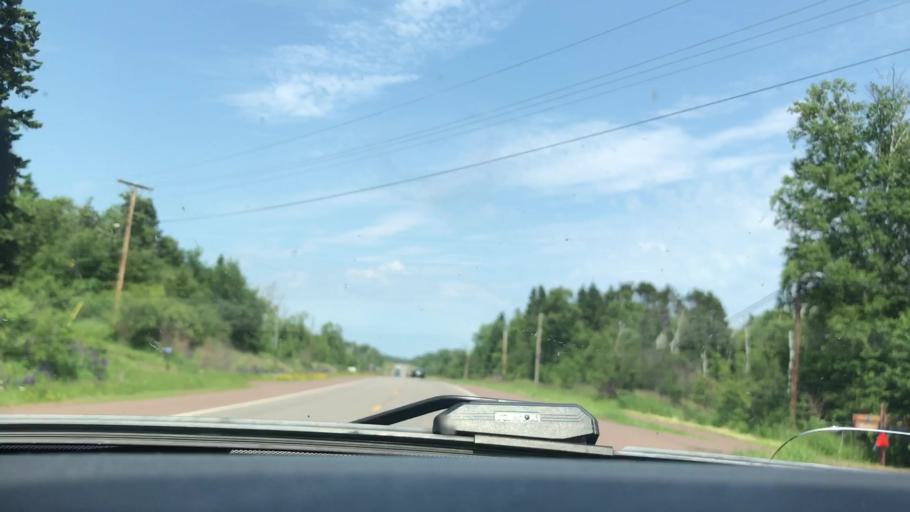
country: US
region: Minnesota
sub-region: Lake County
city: Silver Bay
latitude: 47.5784
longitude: -90.8272
